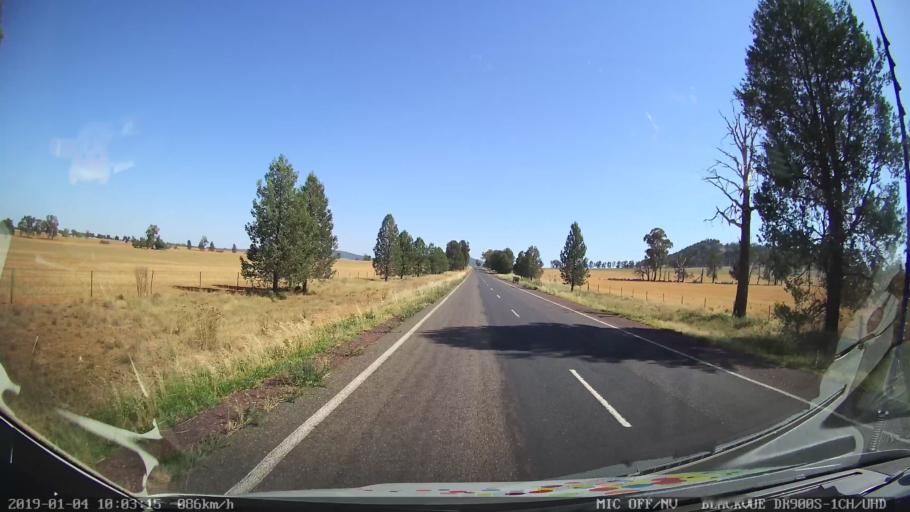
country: AU
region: New South Wales
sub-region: Cabonne
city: Canowindra
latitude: -33.4662
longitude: 148.3646
